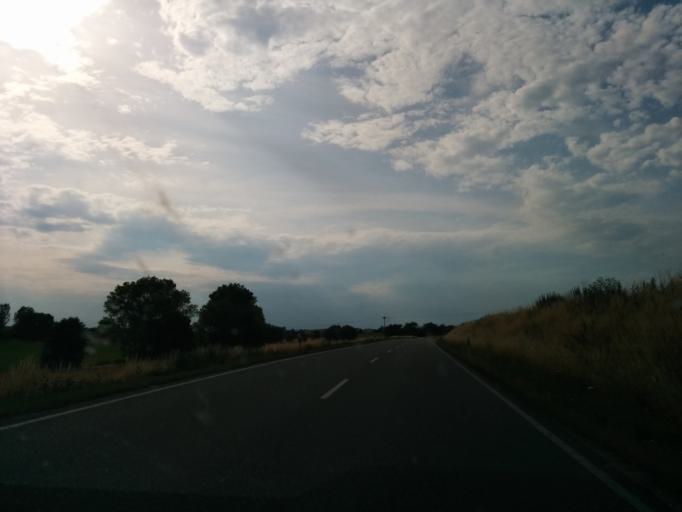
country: DE
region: Thuringia
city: Etzelsrode
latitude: 51.5278
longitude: 10.6274
